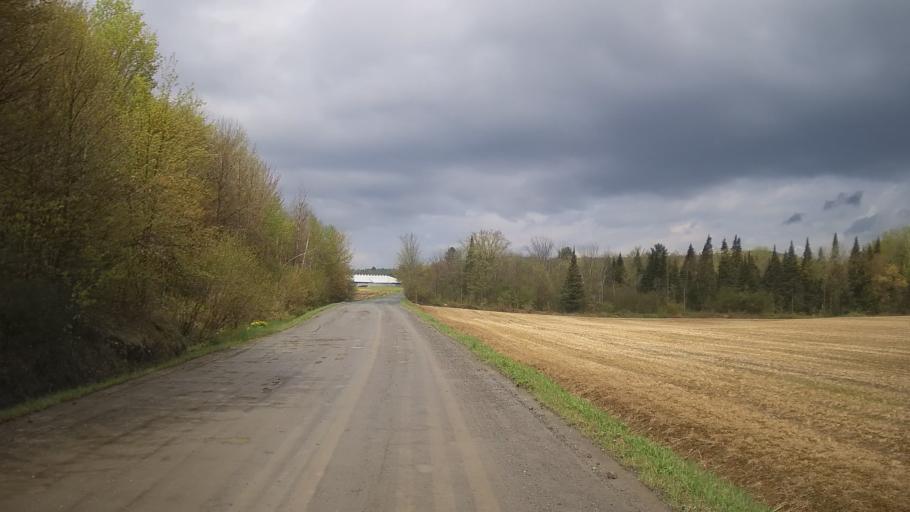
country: CA
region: Quebec
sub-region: Monteregie
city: Cowansville
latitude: 45.1743
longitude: -72.6826
